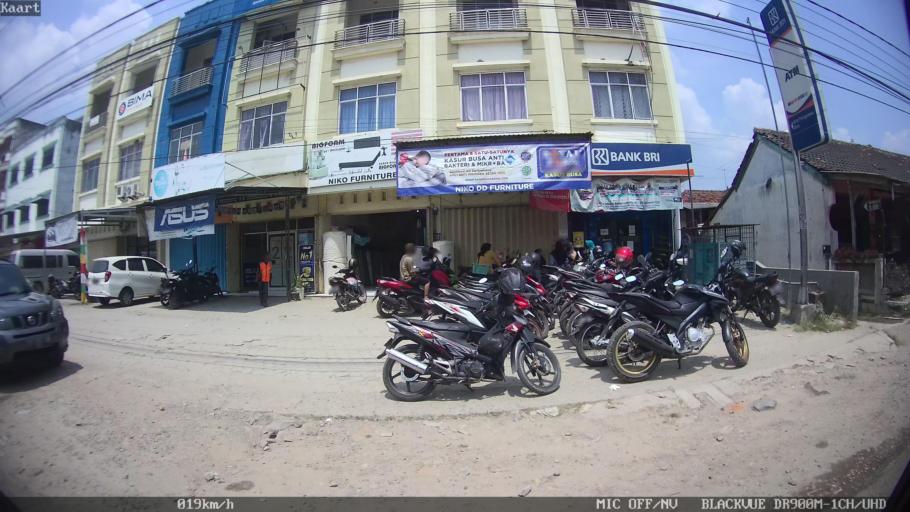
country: ID
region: Lampung
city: Pringsewu
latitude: -5.3509
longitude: 104.9760
